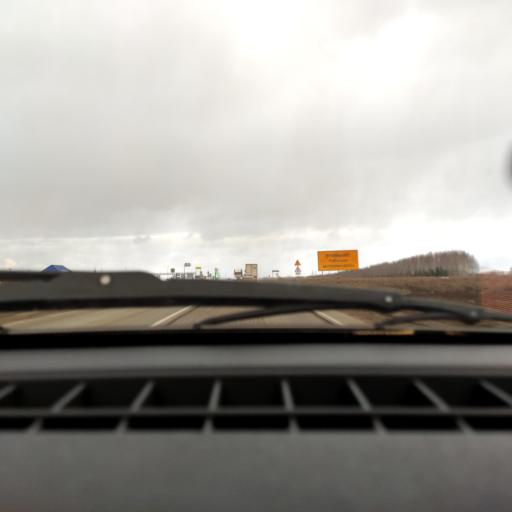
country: RU
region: Bashkortostan
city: Iglino
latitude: 54.7445
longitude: 56.3110
